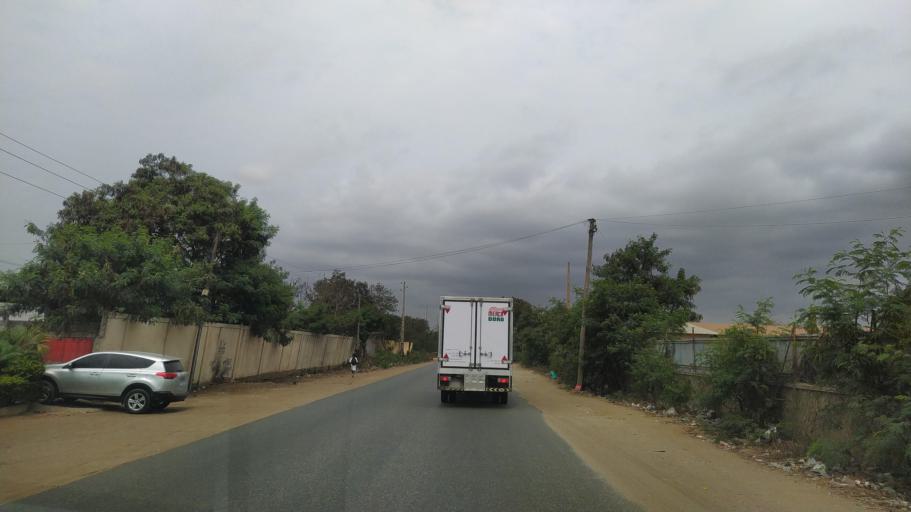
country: AO
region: Luanda
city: Luanda
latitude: -8.8578
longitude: 13.2826
